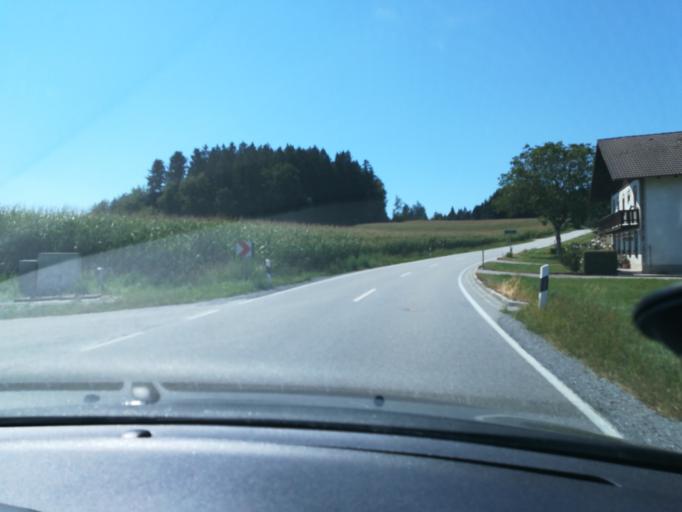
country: DE
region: Bavaria
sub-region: Upper Bavaria
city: Amerang
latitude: 48.0325
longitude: 12.3049
